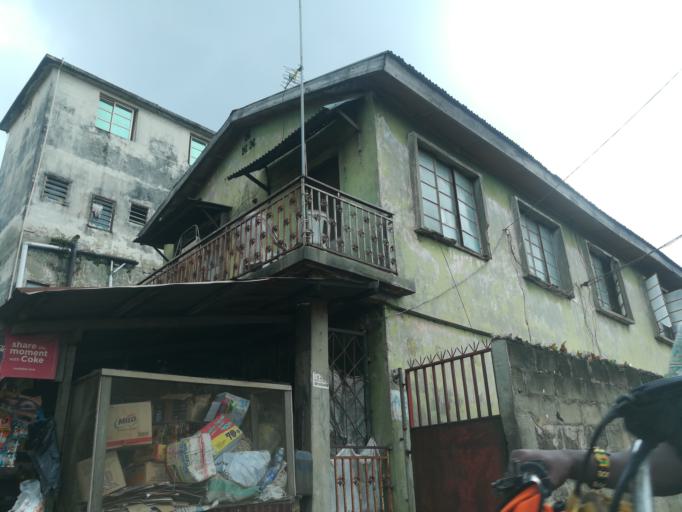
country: NG
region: Lagos
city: Mushin
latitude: 6.5300
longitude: 3.3630
